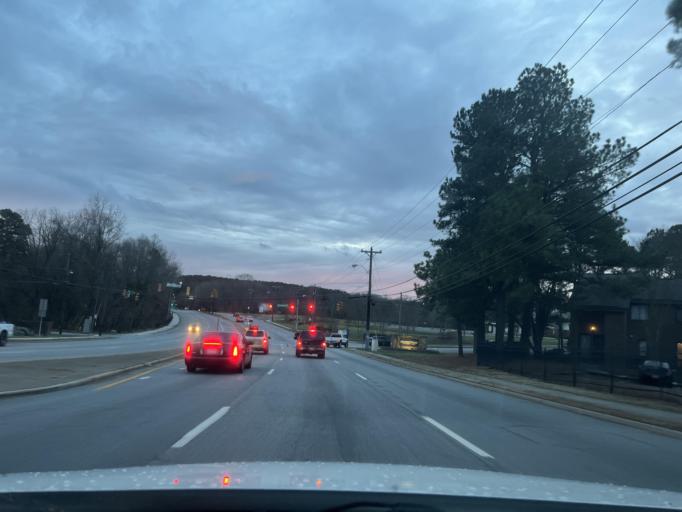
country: US
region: North Carolina
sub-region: Guilford County
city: Greensboro
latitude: 36.0339
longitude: -79.8501
